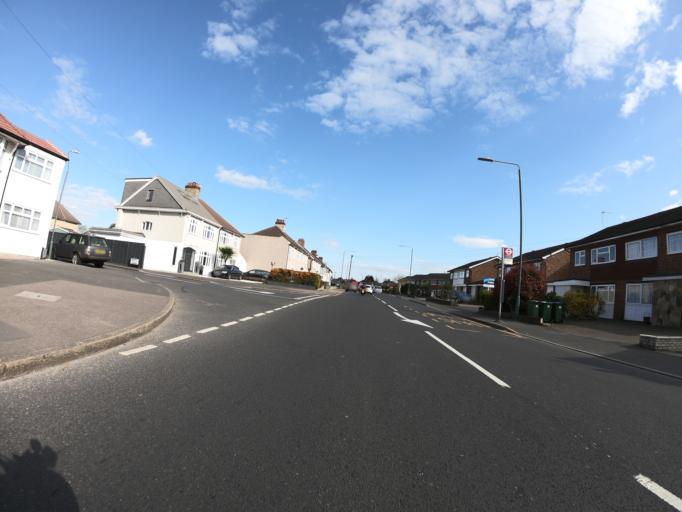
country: GB
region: England
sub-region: Greater London
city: Bexleyheath
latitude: 51.4726
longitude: 0.1322
